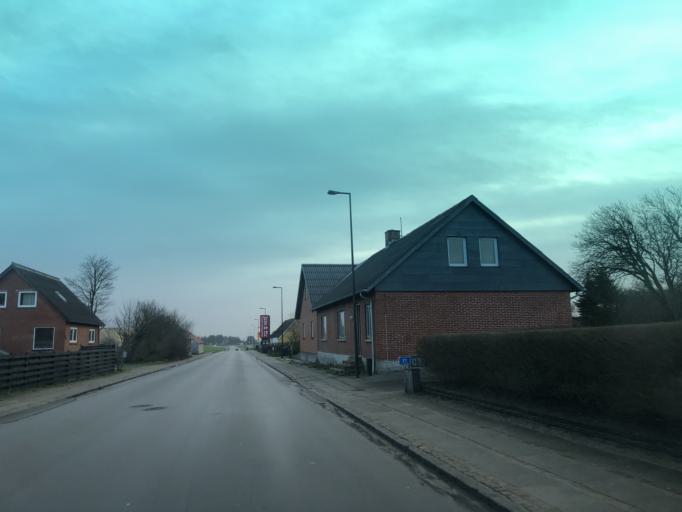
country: DK
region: North Denmark
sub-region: Thisted Kommune
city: Hurup
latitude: 56.7461
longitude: 8.4308
